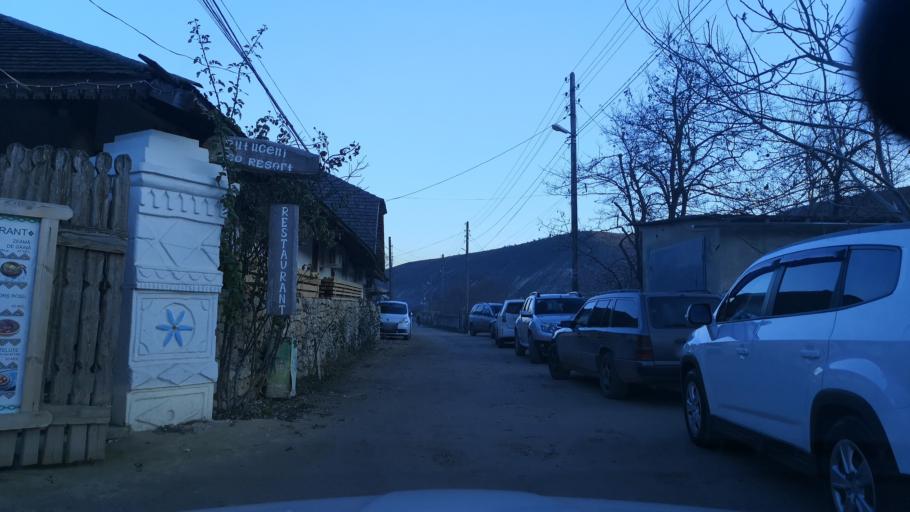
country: MD
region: Telenesti
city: Cocieri
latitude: 47.3017
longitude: 28.9674
